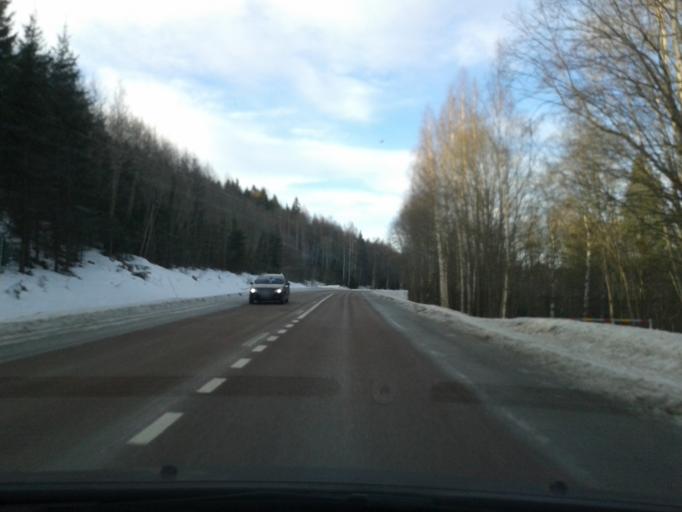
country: SE
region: Vaesternorrland
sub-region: OErnskoeldsviks Kommun
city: Bjasta
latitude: 63.3421
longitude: 18.5048
